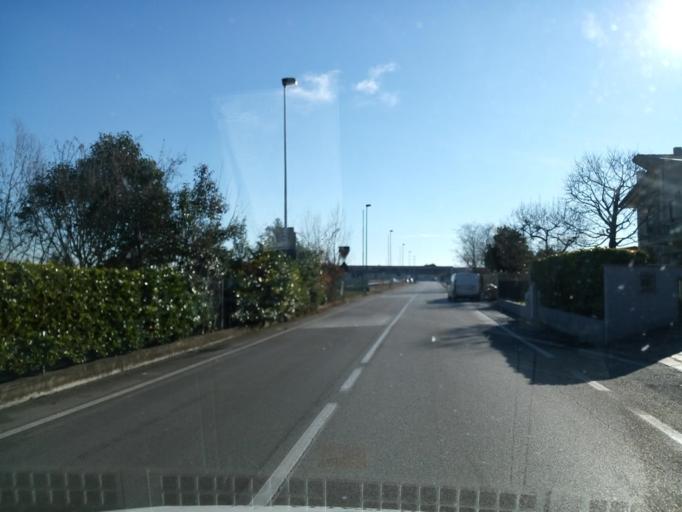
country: IT
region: Veneto
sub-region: Provincia di Treviso
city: Susegana
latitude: 45.8594
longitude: 12.2574
